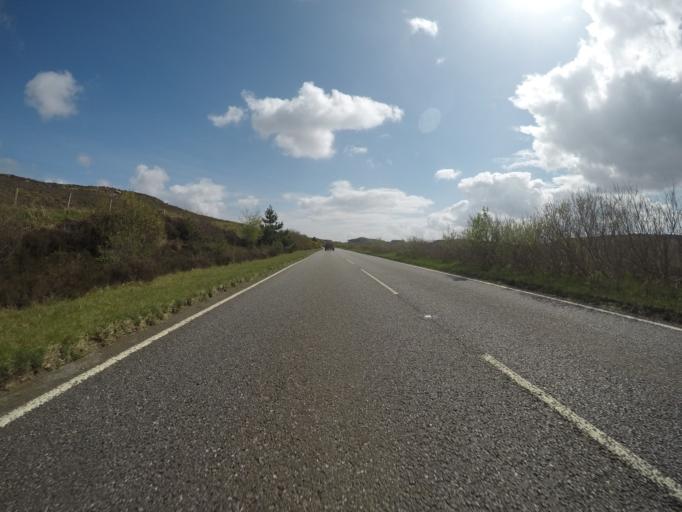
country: GB
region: Scotland
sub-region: Highland
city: Portree
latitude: 57.5252
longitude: -6.3451
